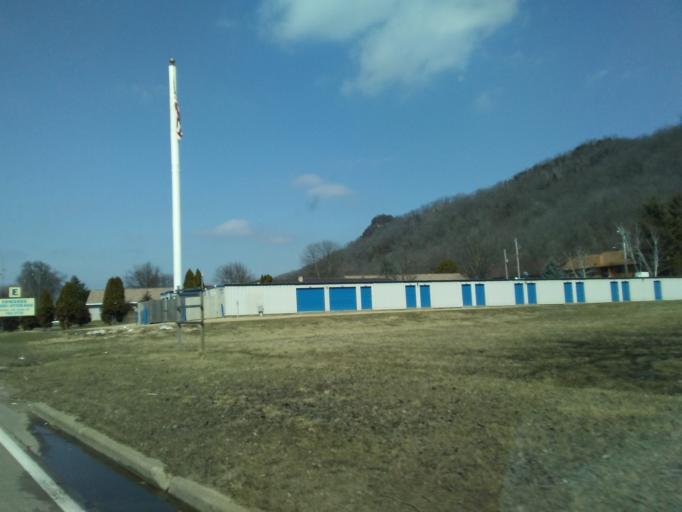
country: US
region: Wisconsin
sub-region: La Crosse County
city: La Crosse
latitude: 43.7570
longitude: -91.2044
